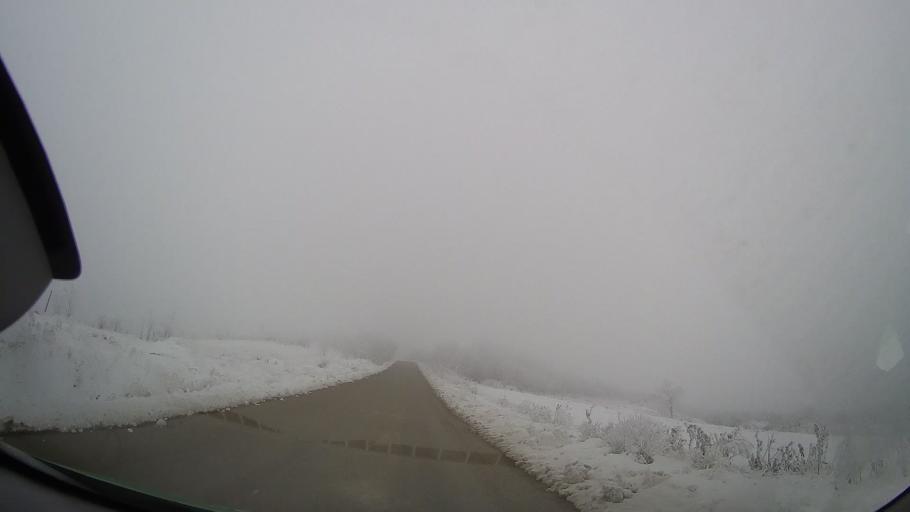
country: RO
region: Iasi
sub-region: Comuna Tansa
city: Suhulet
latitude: 46.8853
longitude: 27.2723
